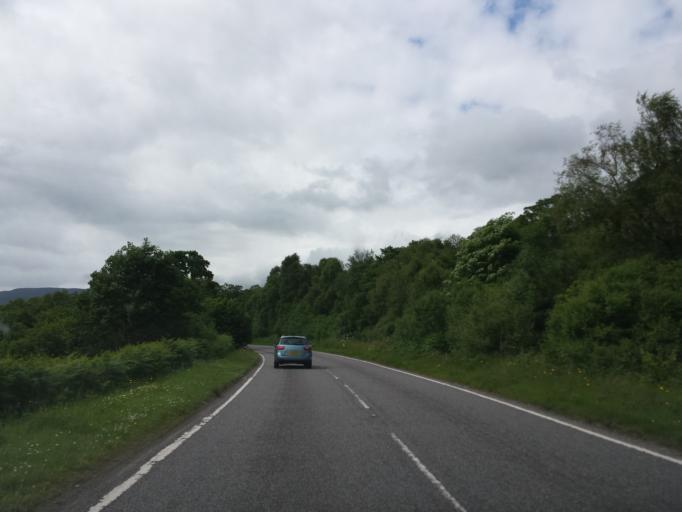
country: GB
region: Scotland
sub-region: Highland
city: Fort William
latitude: 56.8524
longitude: -5.1734
